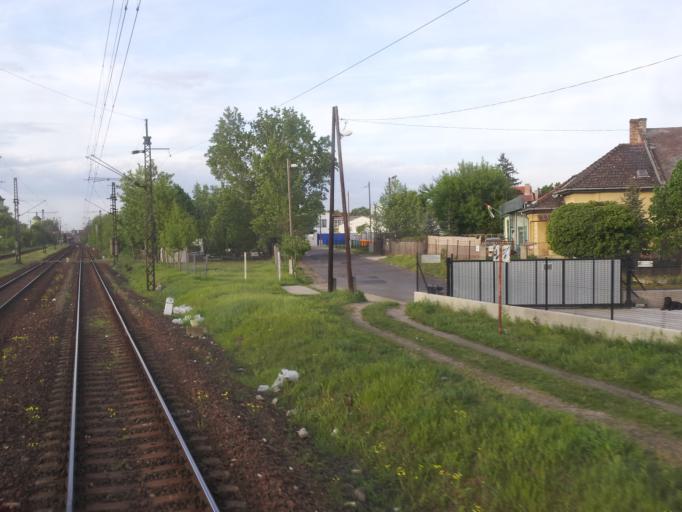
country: HU
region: Budapest
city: Budapest XV. keruelet
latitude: 47.5454
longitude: 19.1048
